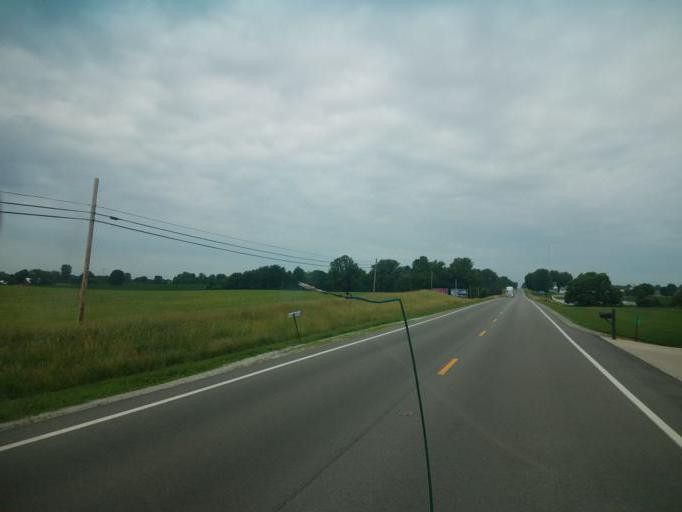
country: US
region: Ohio
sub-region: Hardin County
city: Kenton
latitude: 40.6440
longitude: -83.5542
